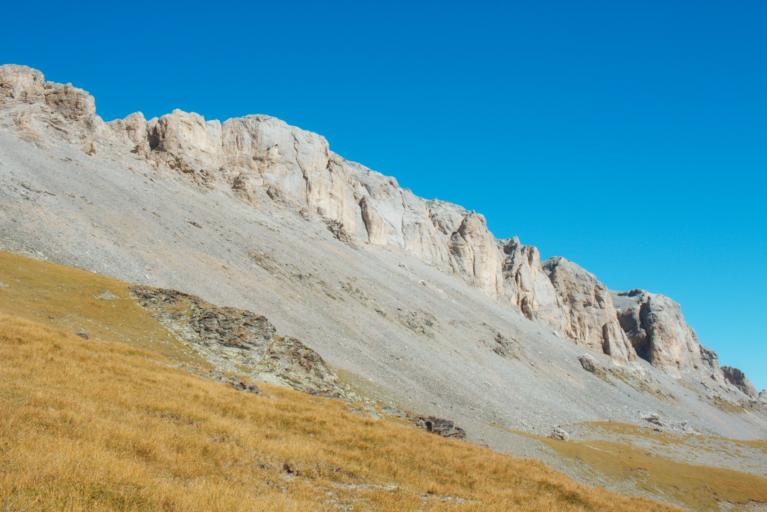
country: RU
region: Karachayevo-Cherkesiya
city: Nizhniy Arkhyz
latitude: 43.5941
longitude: 41.1889
